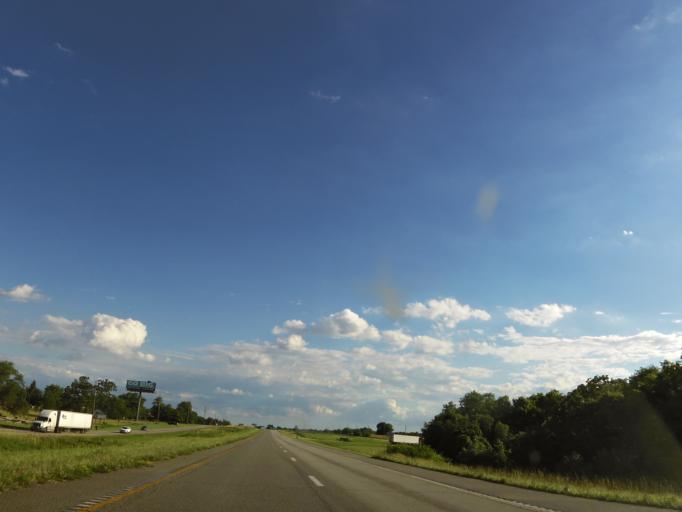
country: US
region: Missouri
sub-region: Lincoln County
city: Troy
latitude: 39.0920
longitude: -90.9688
